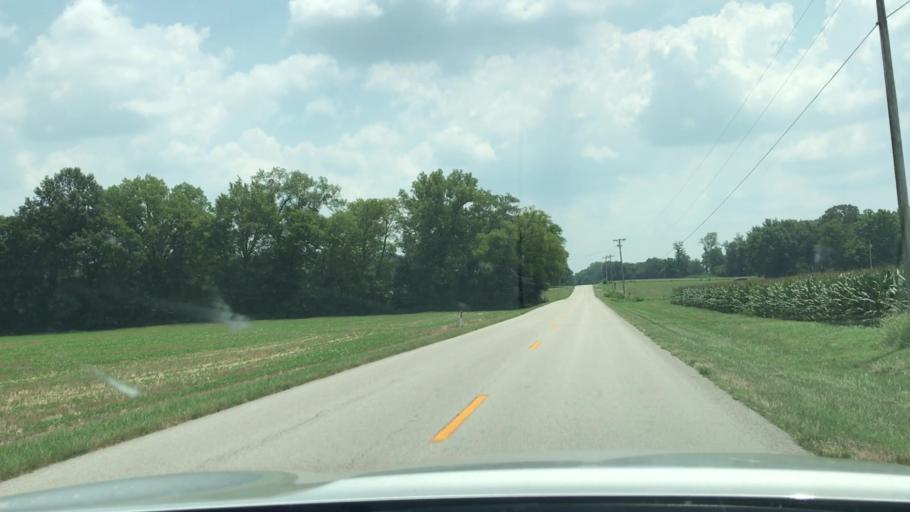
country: US
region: Kentucky
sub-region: Todd County
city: Elkton
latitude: 36.7658
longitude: -87.1098
